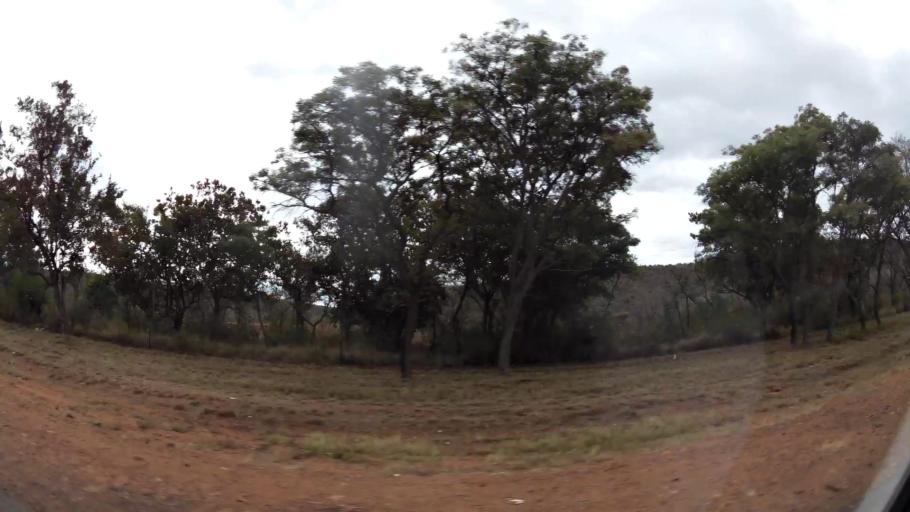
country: ZA
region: Limpopo
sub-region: Waterberg District Municipality
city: Modimolle
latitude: -24.6785
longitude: 28.5272
